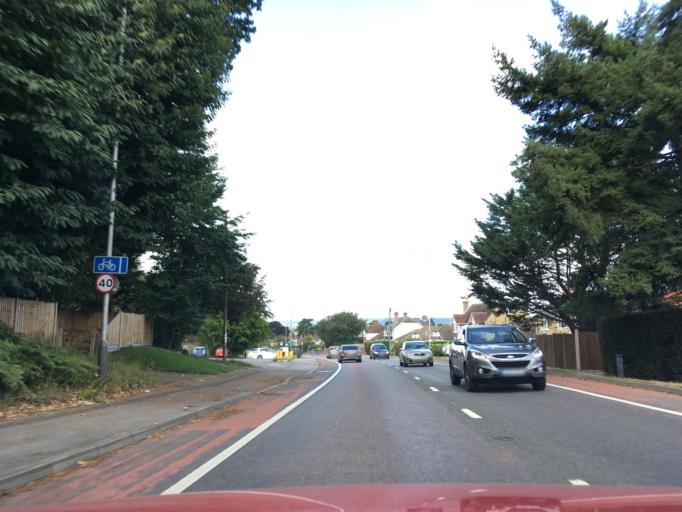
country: GB
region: England
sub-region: Kent
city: Aylesford
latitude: 51.2972
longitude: 0.4625
